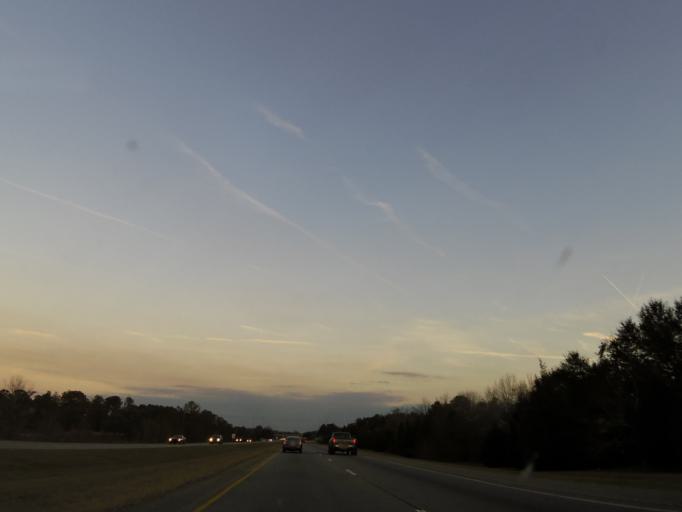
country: US
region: Georgia
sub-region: Dougherty County
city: Albany
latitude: 31.5942
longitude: -84.1340
